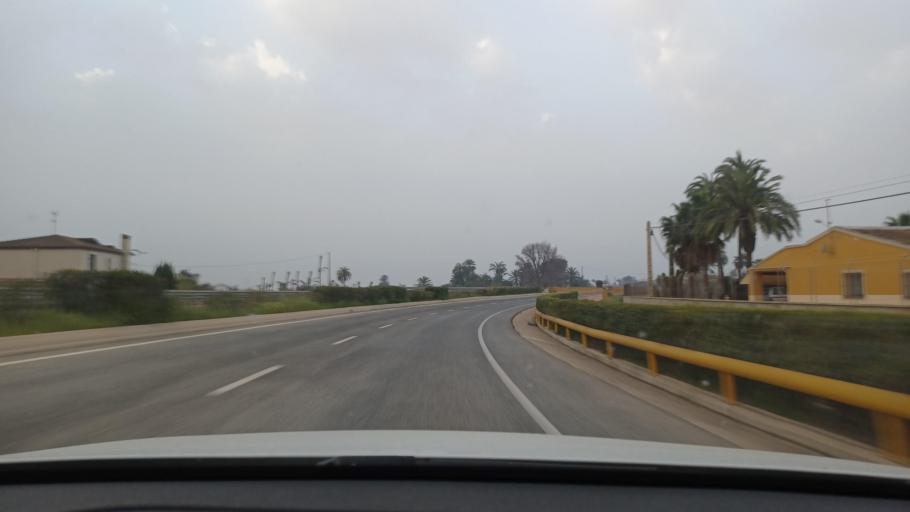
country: ES
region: Valencia
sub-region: Provincia de Alicante
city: Elche
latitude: 38.2094
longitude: -0.6979
